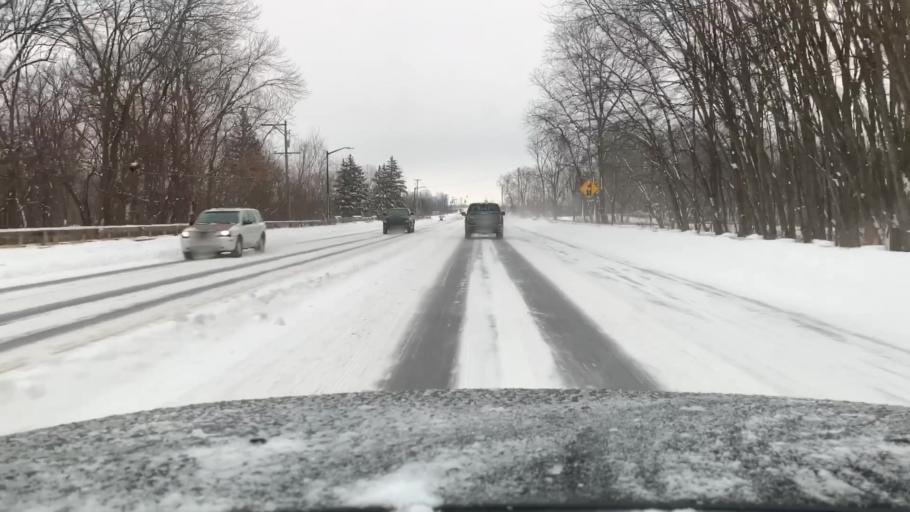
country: US
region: Michigan
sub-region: Ottawa County
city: Zeeland
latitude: 42.7831
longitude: -86.0389
